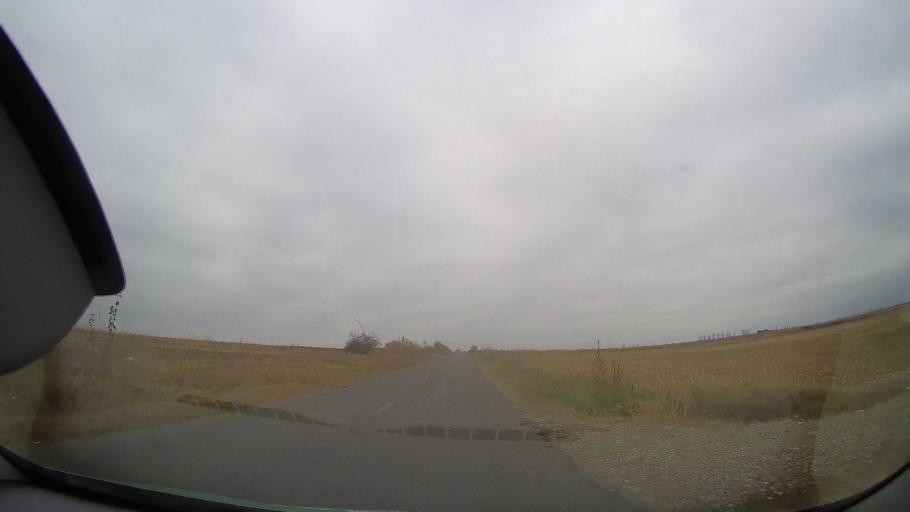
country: RO
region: Buzau
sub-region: Comuna Luciu
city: Luciu
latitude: 44.9776
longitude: 27.0546
